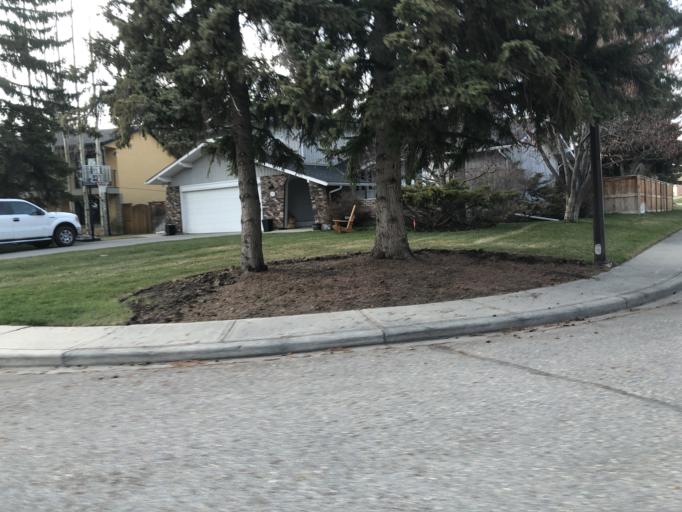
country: CA
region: Alberta
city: Calgary
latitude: 50.9442
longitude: -114.0502
